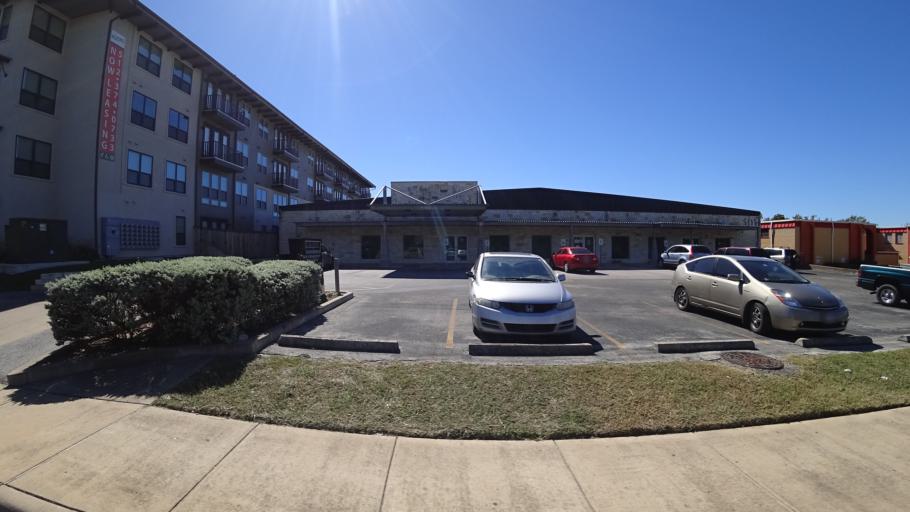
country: US
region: Texas
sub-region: Travis County
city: Austin
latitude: 30.3225
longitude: -97.7199
